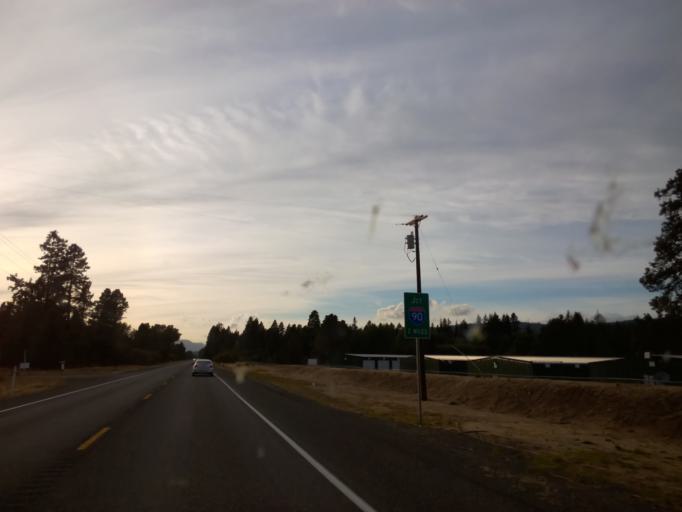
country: US
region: Washington
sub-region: Kittitas County
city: Cle Elum
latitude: 47.1778
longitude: -120.8668
